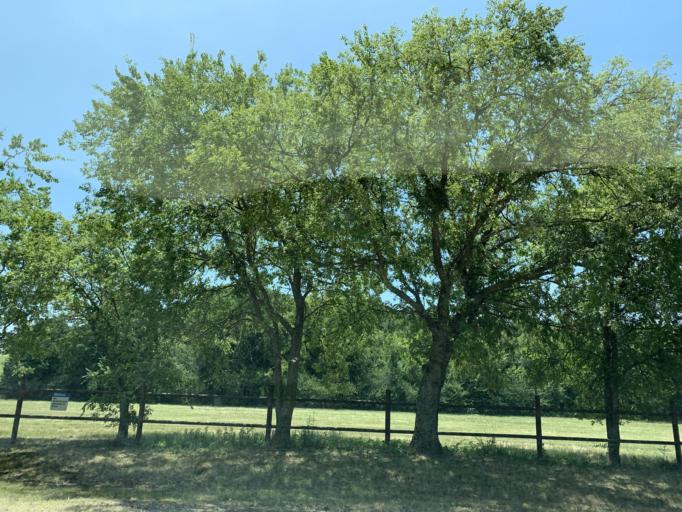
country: US
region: Texas
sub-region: Dallas County
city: Cedar Hill
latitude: 32.6410
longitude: -97.0225
